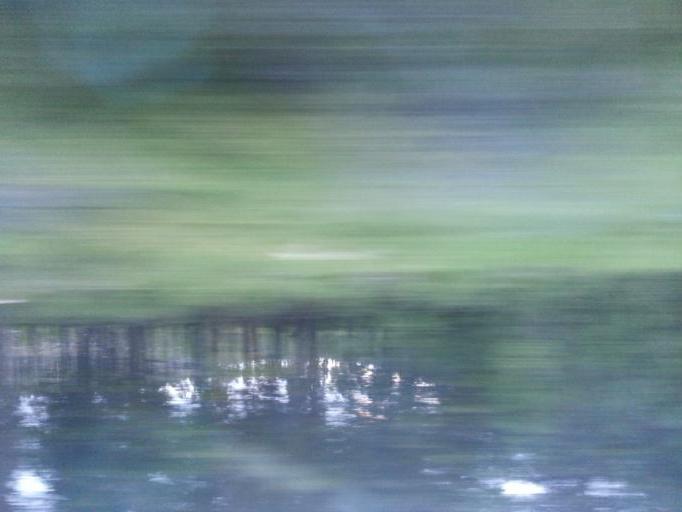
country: NO
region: Oppland
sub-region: Dovre
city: Dombas
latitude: 62.0940
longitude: 9.1367
